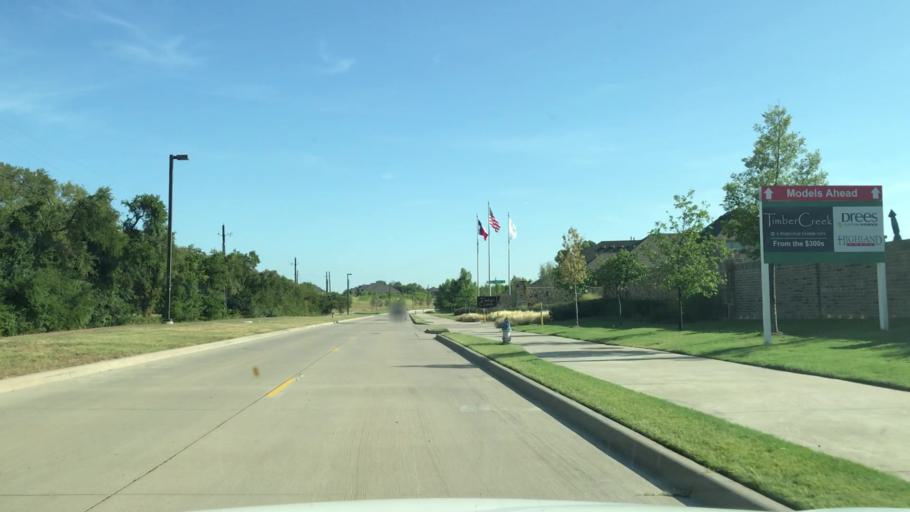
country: US
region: Texas
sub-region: Collin County
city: McKinney
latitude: 33.2351
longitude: -96.6516
